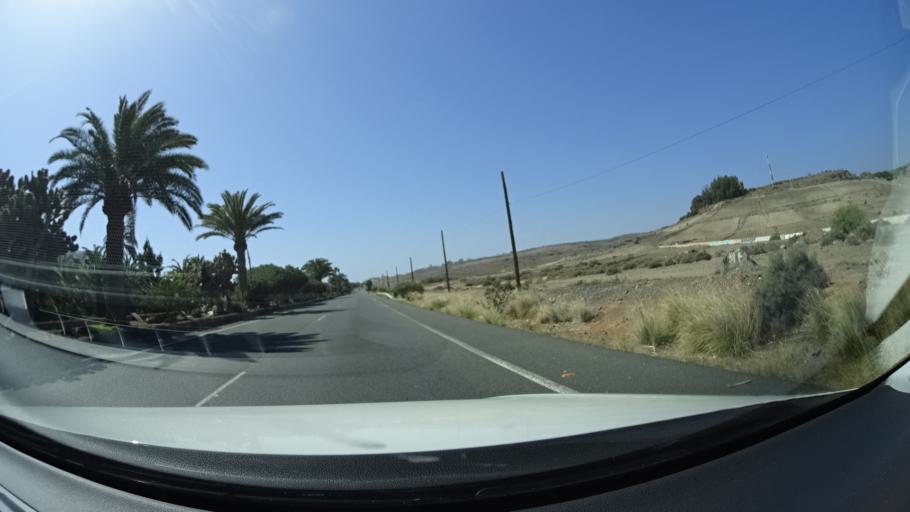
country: ES
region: Canary Islands
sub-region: Provincia de Las Palmas
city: Playa del Ingles
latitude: 27.7821
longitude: -15.5209
